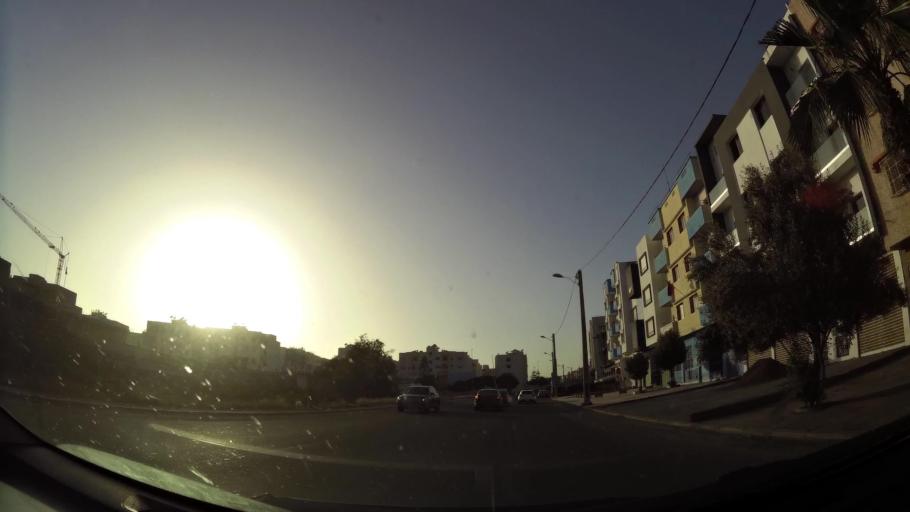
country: MA
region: Oued ed Dahab-Lagouira
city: Dakhla
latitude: 30.3940
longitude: -9.5452
